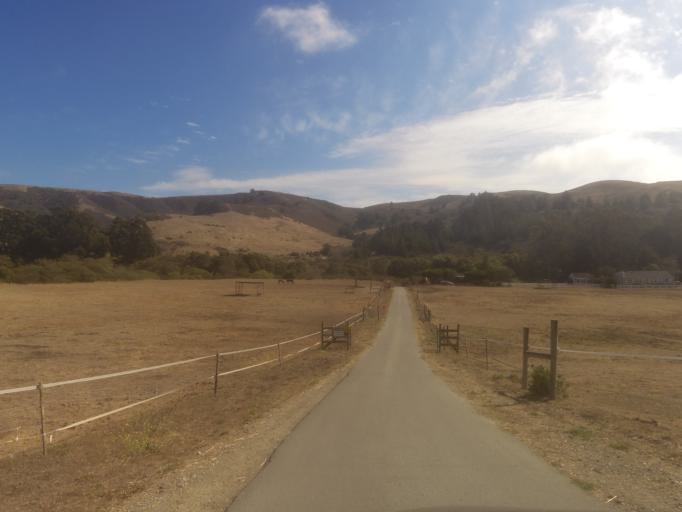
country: US
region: California
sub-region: San Mateo County
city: Half Moon Bay
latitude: 37.4173
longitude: -122.3986
